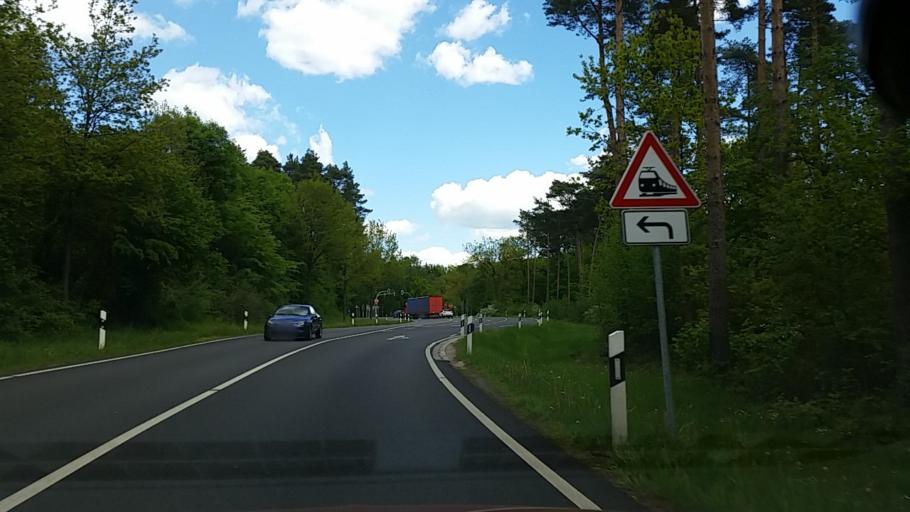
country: DE
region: Lower Saxony
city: Gifhorn
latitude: 52.4953
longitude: 10.5689
